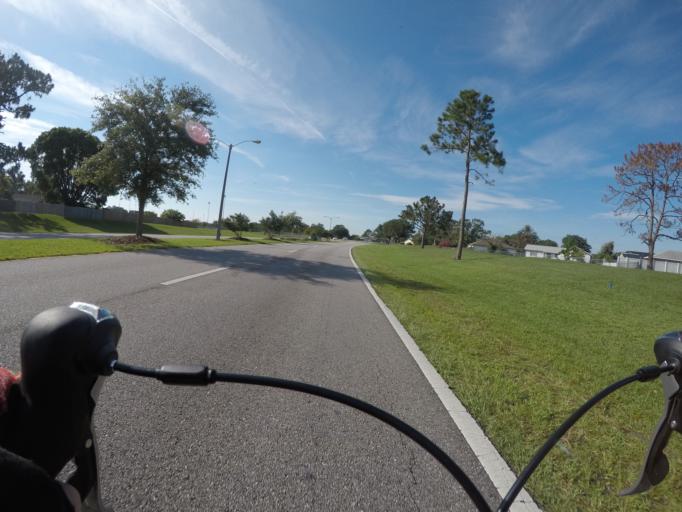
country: US
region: Florida
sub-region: Osceola County
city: Buenaventura Lakes
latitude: 28.3361
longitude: -81.3568
